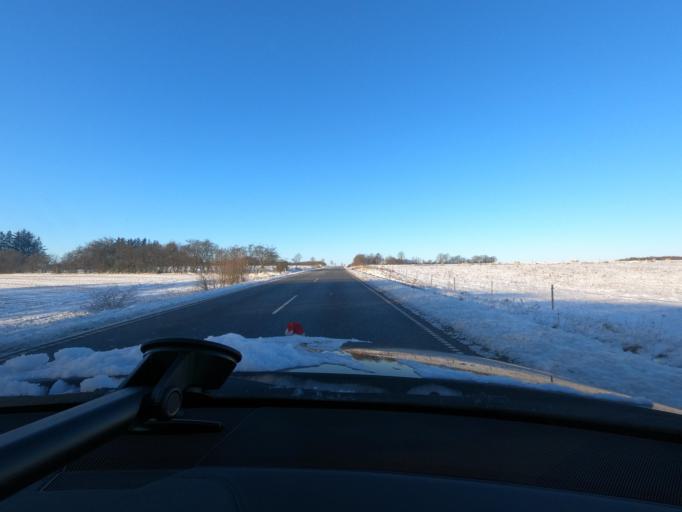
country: DK
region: South Denmark
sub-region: Tonder Kommune
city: Toftlund
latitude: 55.1188
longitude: 9.1584
